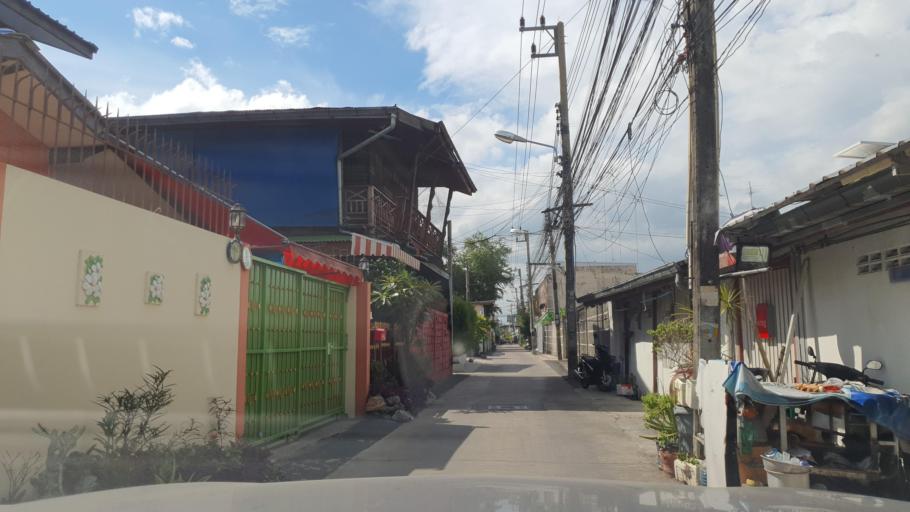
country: TH
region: Chon Buri
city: Chon Buri
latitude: 13.3696
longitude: 100.9851
